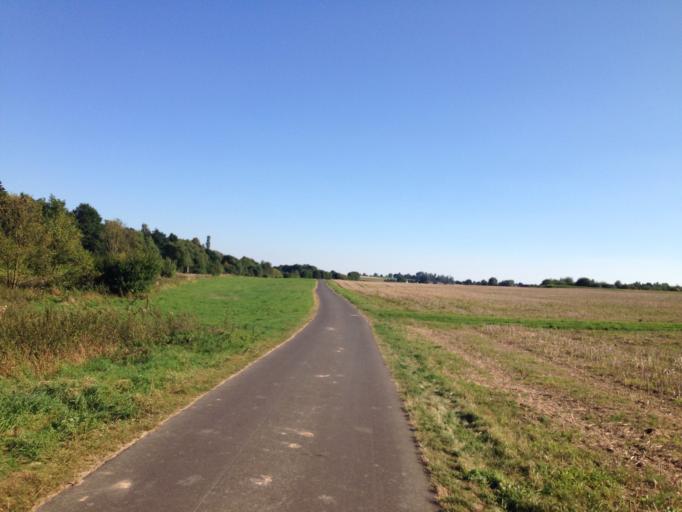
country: DE
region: Hesse
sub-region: Regierungsbezirk Giessen
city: Grunberg
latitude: 50.6295
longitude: 8.9386
